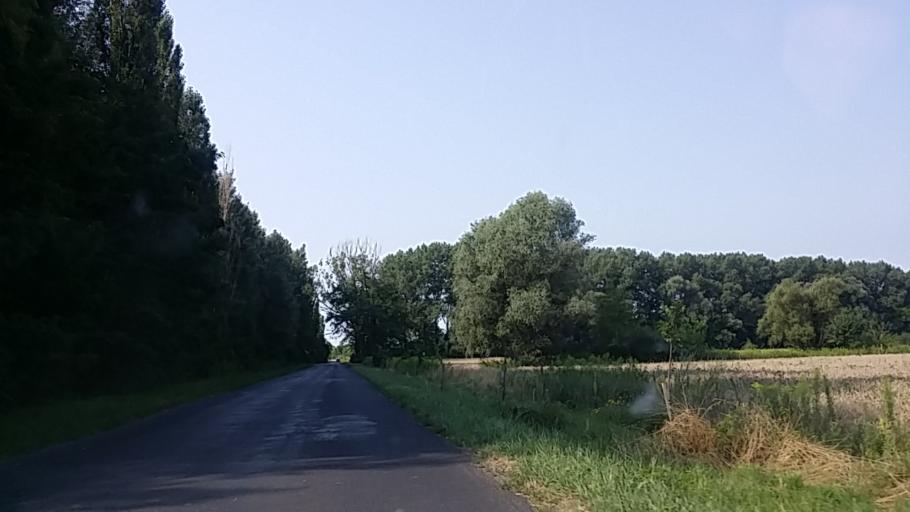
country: HU
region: Veszprem
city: Badacsonytomaj
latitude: 46.8247
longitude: 17.4808
